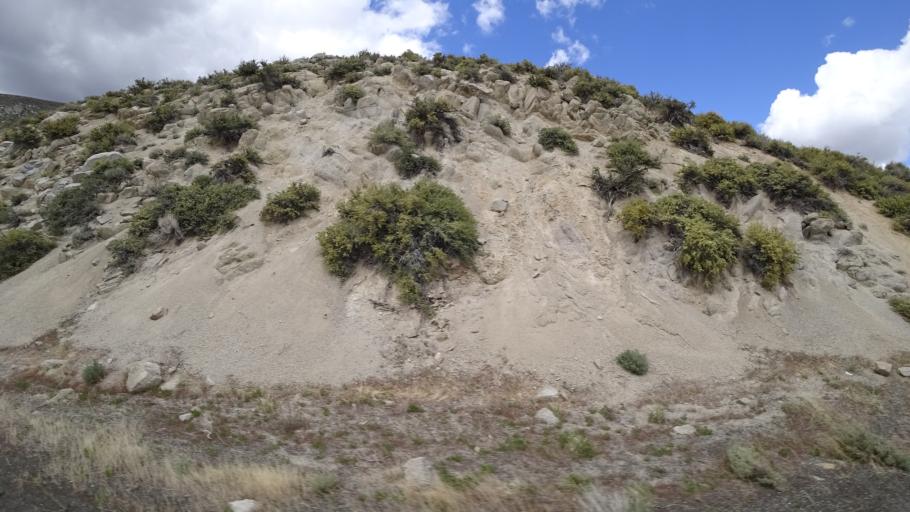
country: US
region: California
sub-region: Mono County
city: Bridgeport
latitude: 38.0782
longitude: -119.1630
